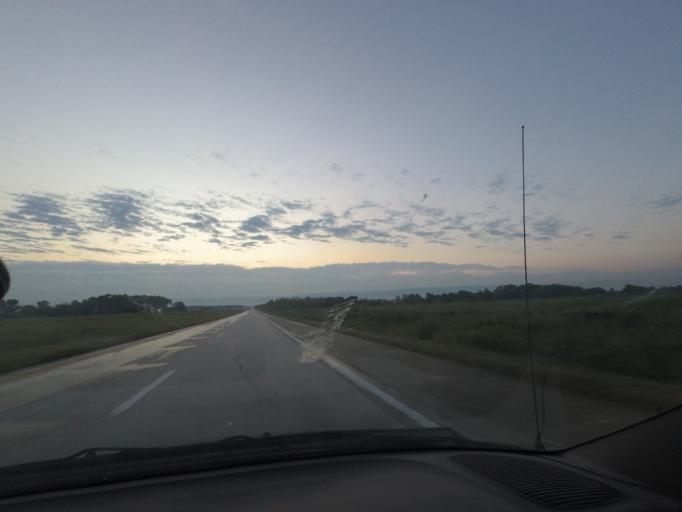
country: US
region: Missouri
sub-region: Macon County
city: Macon
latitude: 39.7603
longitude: -92.6966
